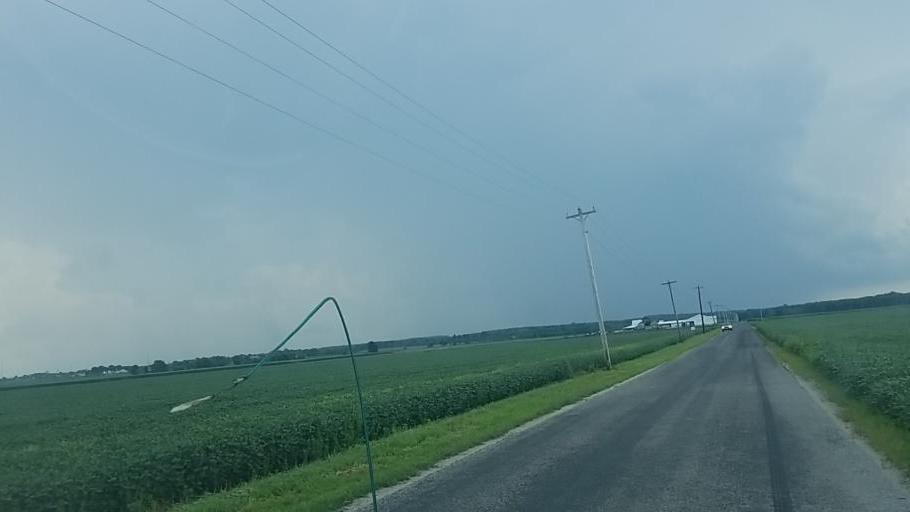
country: US
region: Ohio
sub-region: Medina County
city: Lodi
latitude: 41.0141
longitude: -82.0184
